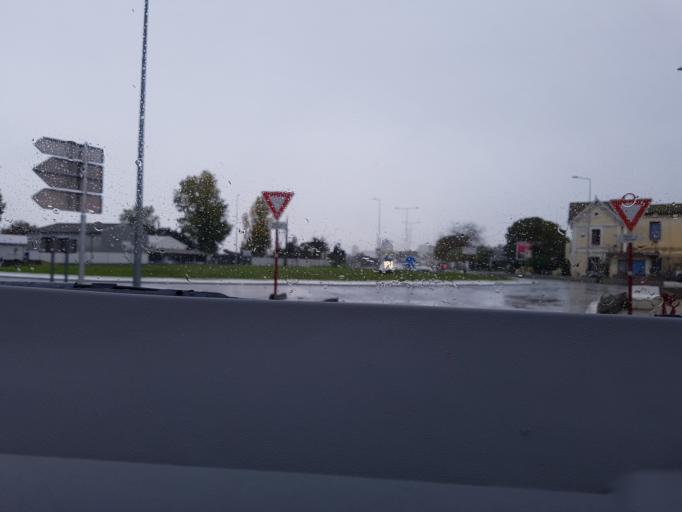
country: FR
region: Aquitaine
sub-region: Departement de la Gironde
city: Bassens
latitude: 44.8991
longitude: -0.5320
